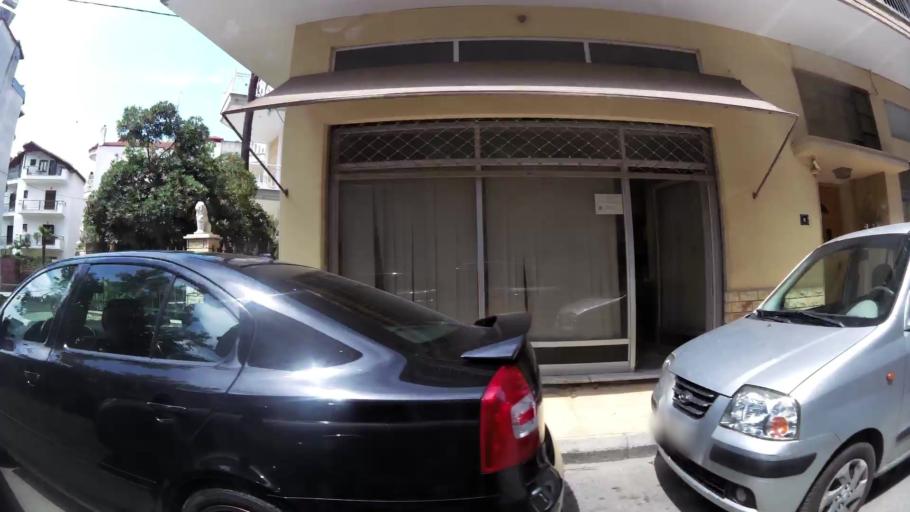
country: GR
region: Central Macedonia
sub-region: Nomos Pierias
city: Katerini
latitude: 40.2706
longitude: 22.5031
